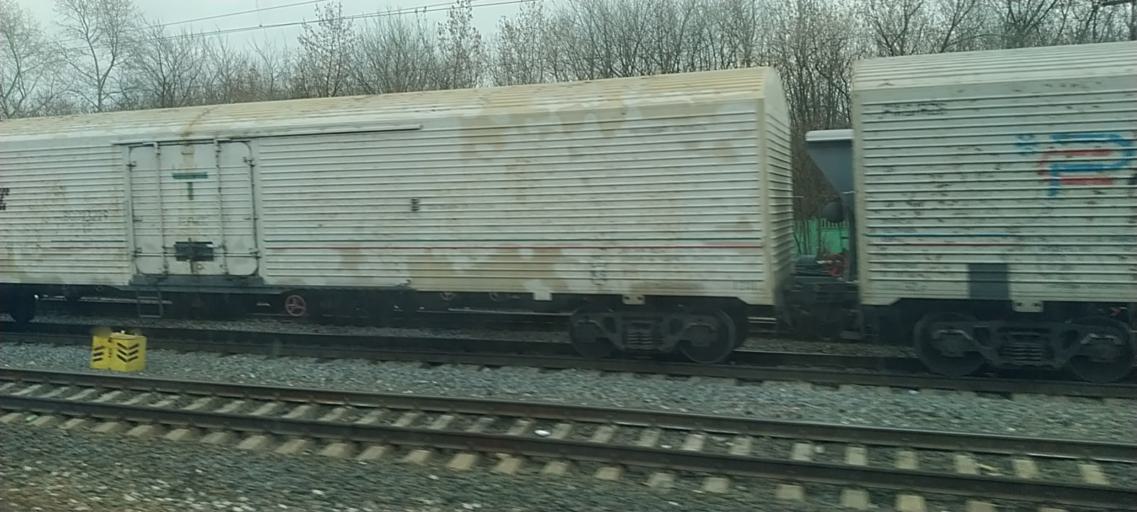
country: RU
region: Moskovskaya
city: Tomilino
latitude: 55.6724
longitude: 37.9417
